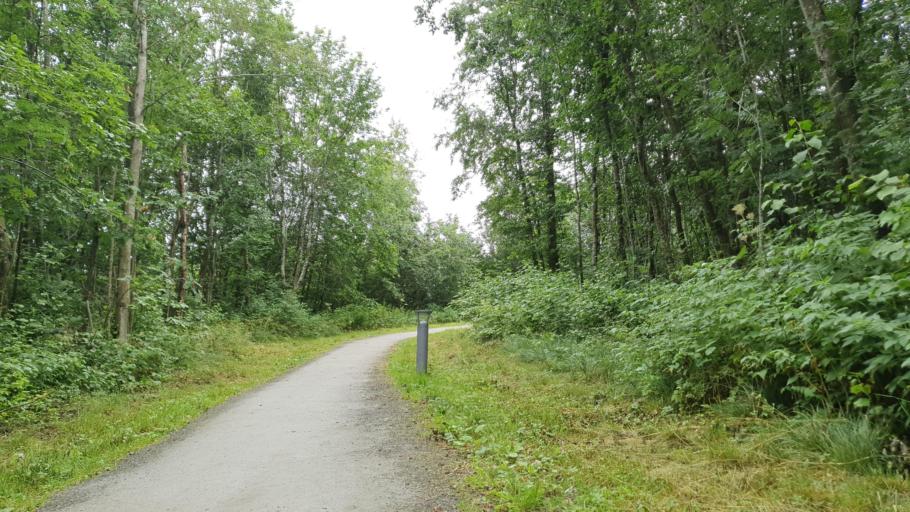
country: NO
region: Sor-Trondelag
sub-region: Selbu
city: Mebonden
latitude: 63.2310
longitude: 11.0238
